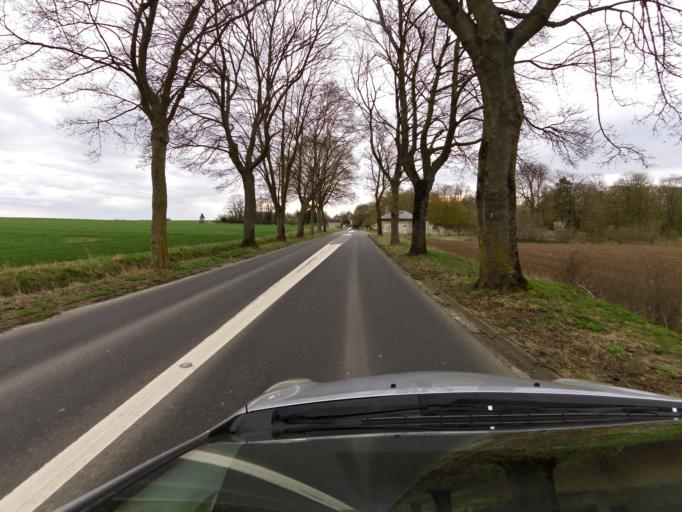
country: FR
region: Picardie
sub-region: Departement de l'Oise
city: Chamant
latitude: 49.1971
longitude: 2.6217
